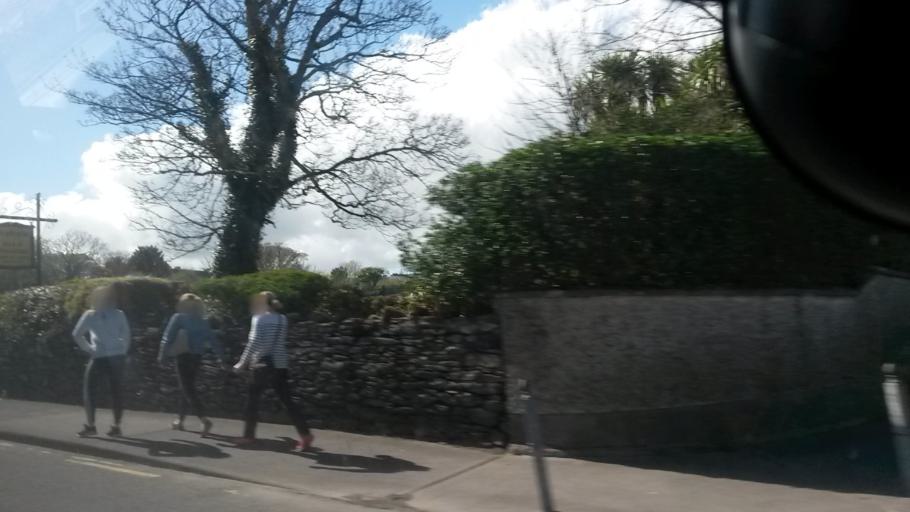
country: IE
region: Munster
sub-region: Ciarrai
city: Dingle
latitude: 52.1419
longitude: -10.2648
